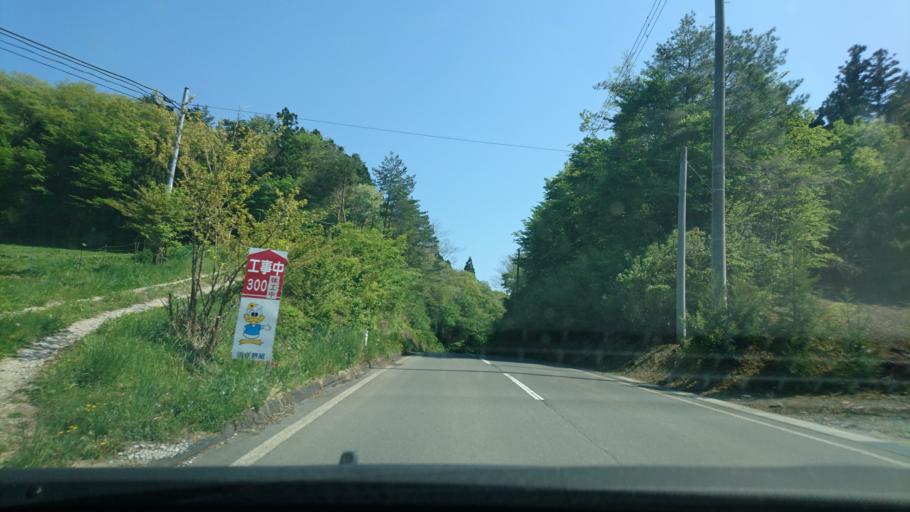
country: JP
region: Iwate
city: Ichinoseki
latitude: 38.9247
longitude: 141.2774
